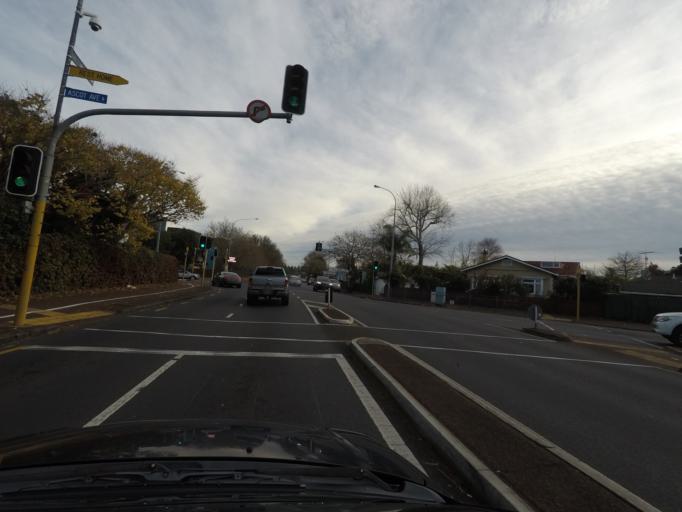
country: NZ
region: Auckland
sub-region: Auckland
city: Auckland
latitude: -36.8863
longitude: 174.8016
